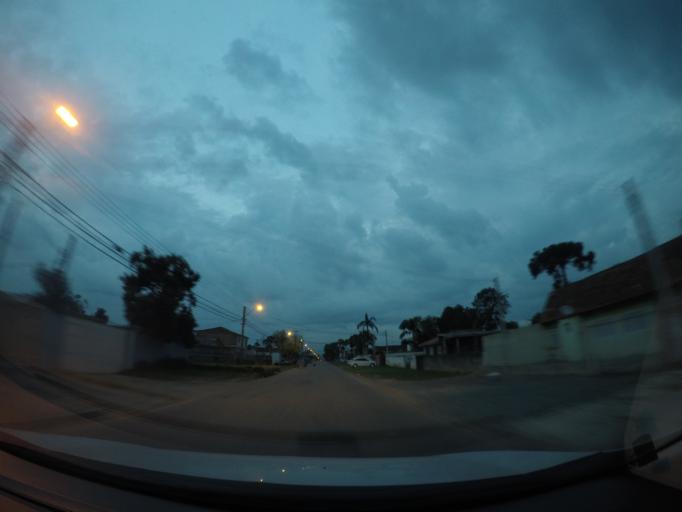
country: BR
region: Parana
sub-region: Sao Jose Dos Pinhais
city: Sao Jose dos Pinhais
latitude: -25.5016
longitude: -49.2320
